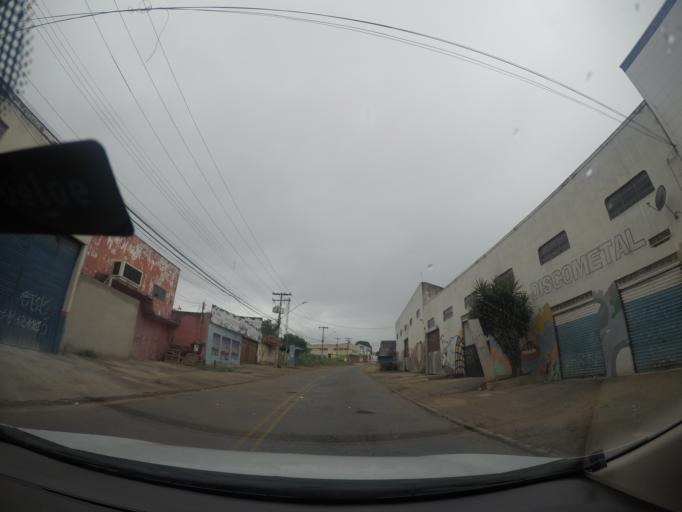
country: BR
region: Goias
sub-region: Goiania
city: Goiania
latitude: -16.6554
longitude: -49.3166
